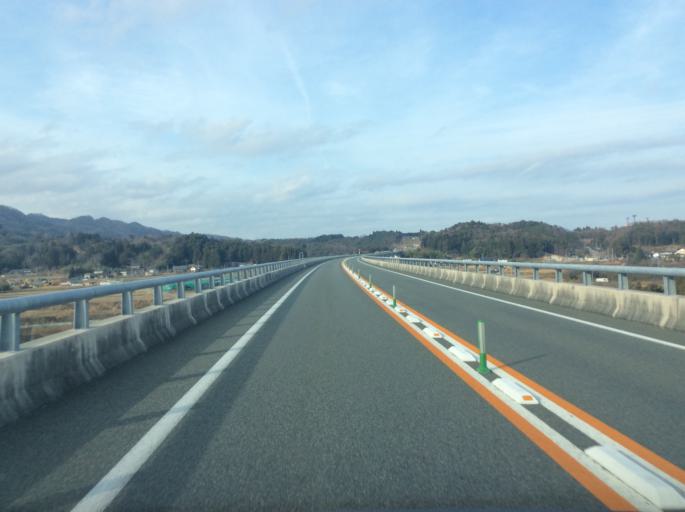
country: JP
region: Fukushima
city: Namie
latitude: 37.2763
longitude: 140.9822
